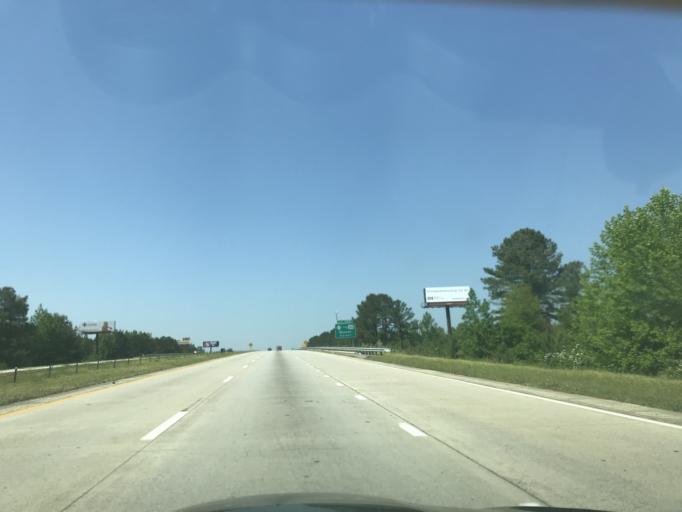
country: US
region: North Carolina
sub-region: Johnston County
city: Benson
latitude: 35.4016
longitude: -78.5231
